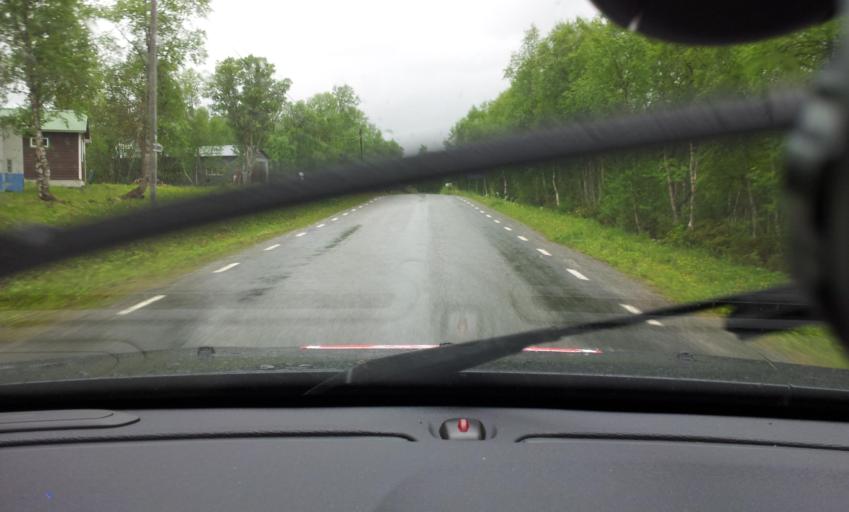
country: SE
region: Jaemtland
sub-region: Are Kommun
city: Are
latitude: 63.1472
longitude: 12.9703
